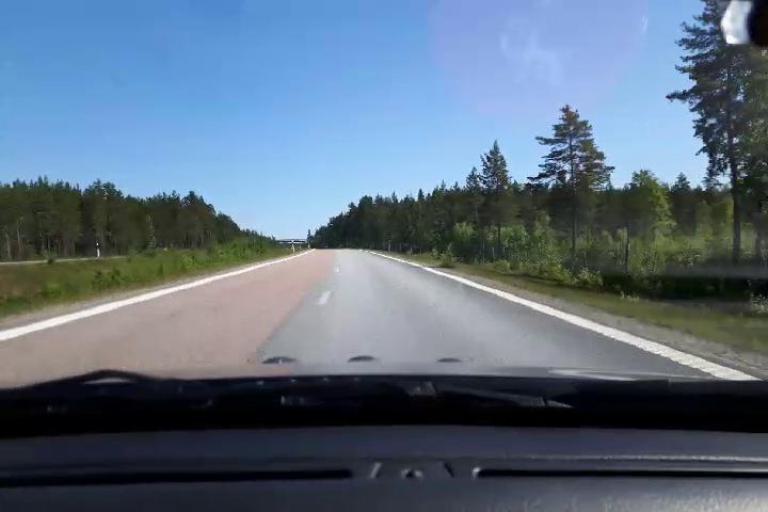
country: SE
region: Gaevleborg
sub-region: Soderhamns Kommun
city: Soderhamn
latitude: 61.3754
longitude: 16.9979
